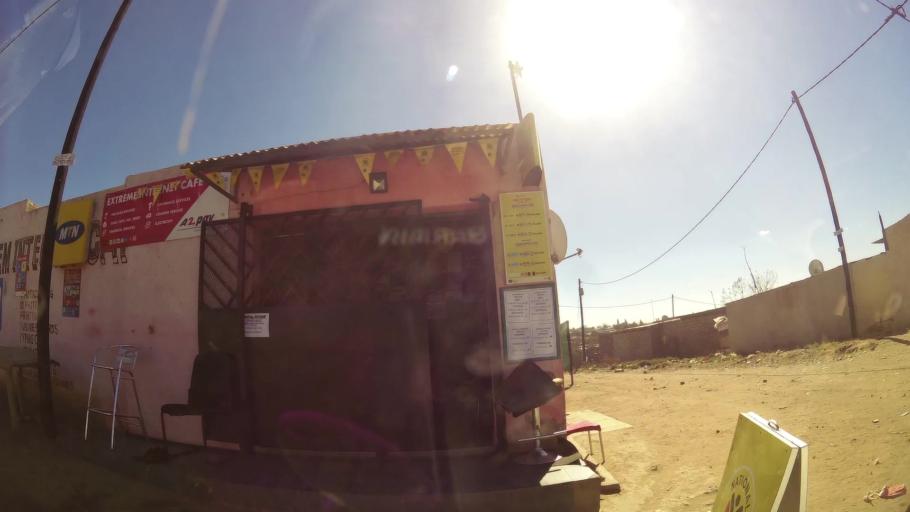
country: ZA
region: Gauteng
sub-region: City of Johannesburg Metropolitan Municipality
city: Diepsloot
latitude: -25.9193
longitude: 28.0886
